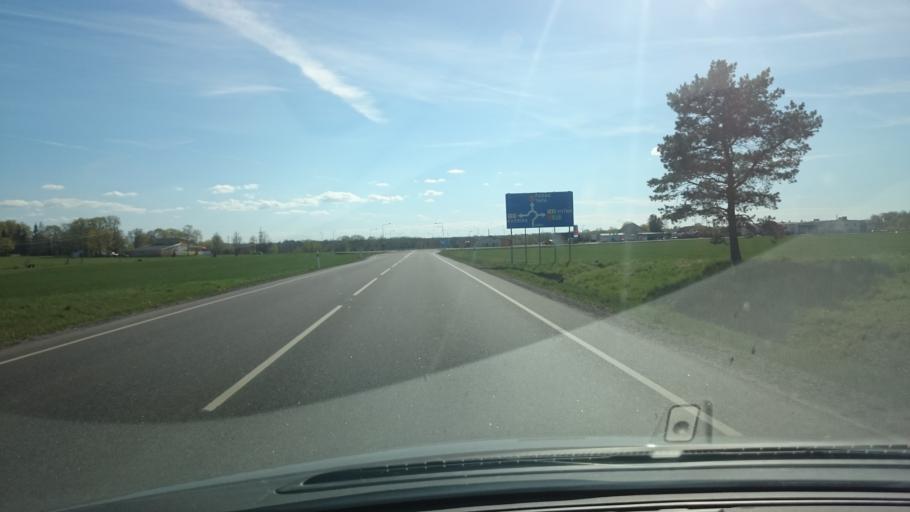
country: EE
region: Laeaene-Virumaa
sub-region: Kadrina vald
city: Kadrina
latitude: 59.3474
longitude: 26.1317
